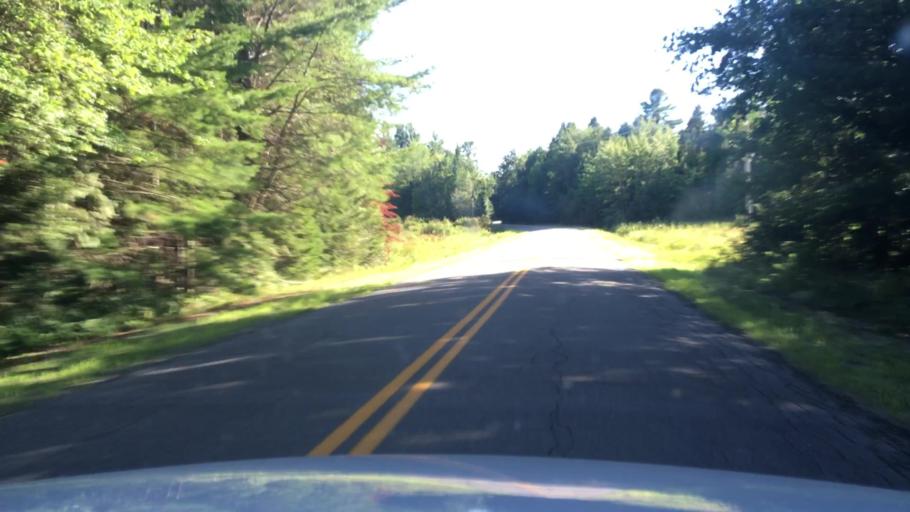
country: US
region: Maine
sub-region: Penobscot County
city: Enfield
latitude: 45.2102
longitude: -68.5905
